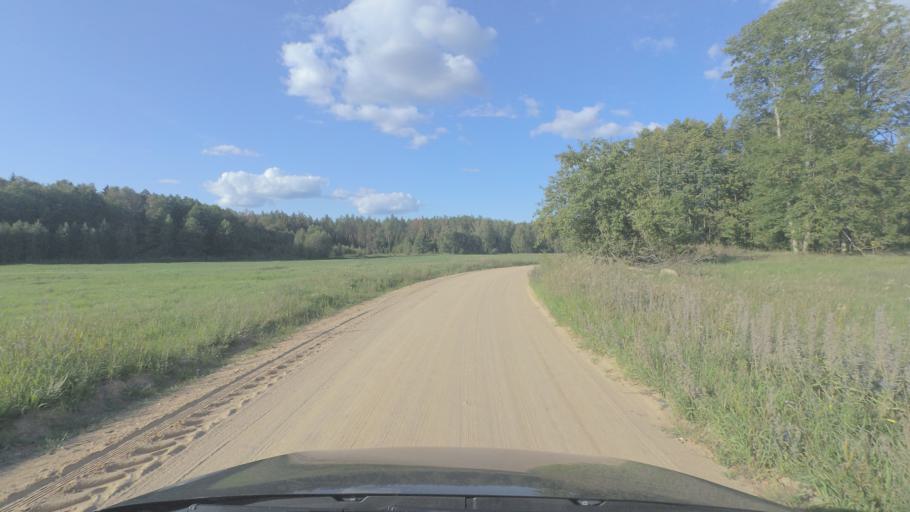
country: LT
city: Pabrade
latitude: 55.1414
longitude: 25.7371
